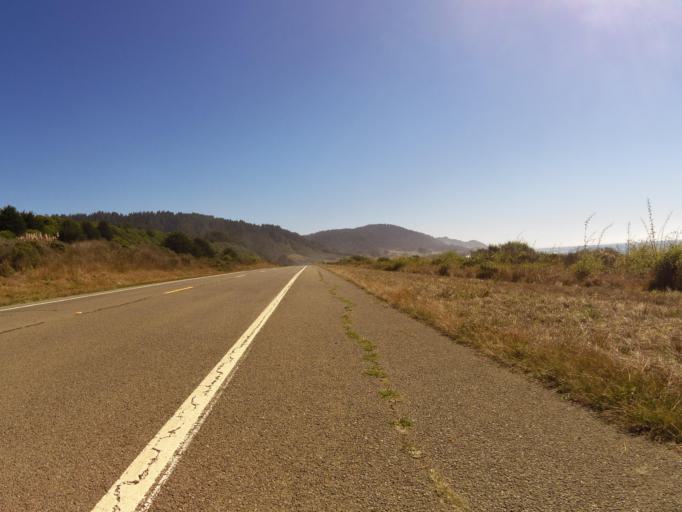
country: US
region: California
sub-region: Mendocino County
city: Fort Bragg
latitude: 39.6667
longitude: -123.7890
